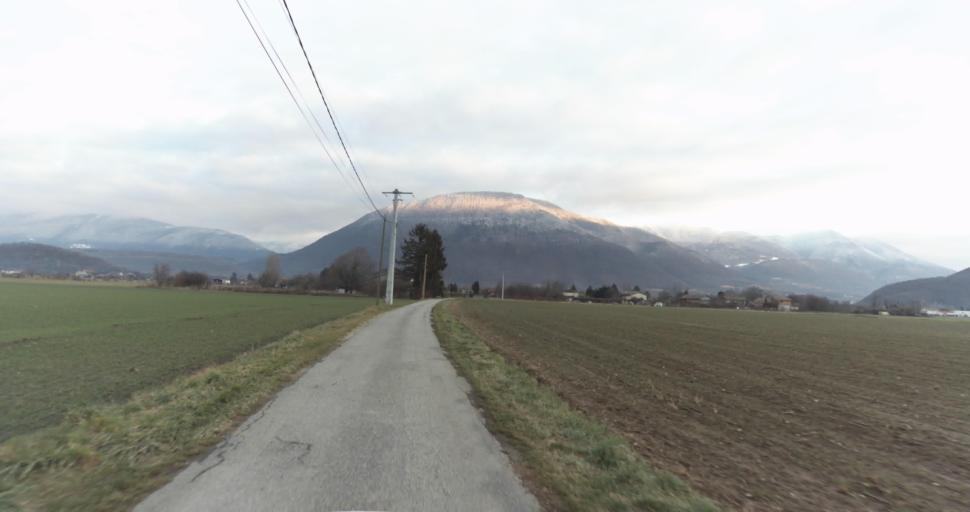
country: FR
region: Rhone-Alpes
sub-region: Departement de l'Isere
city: Vif
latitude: 45.0749
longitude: 5.6908
